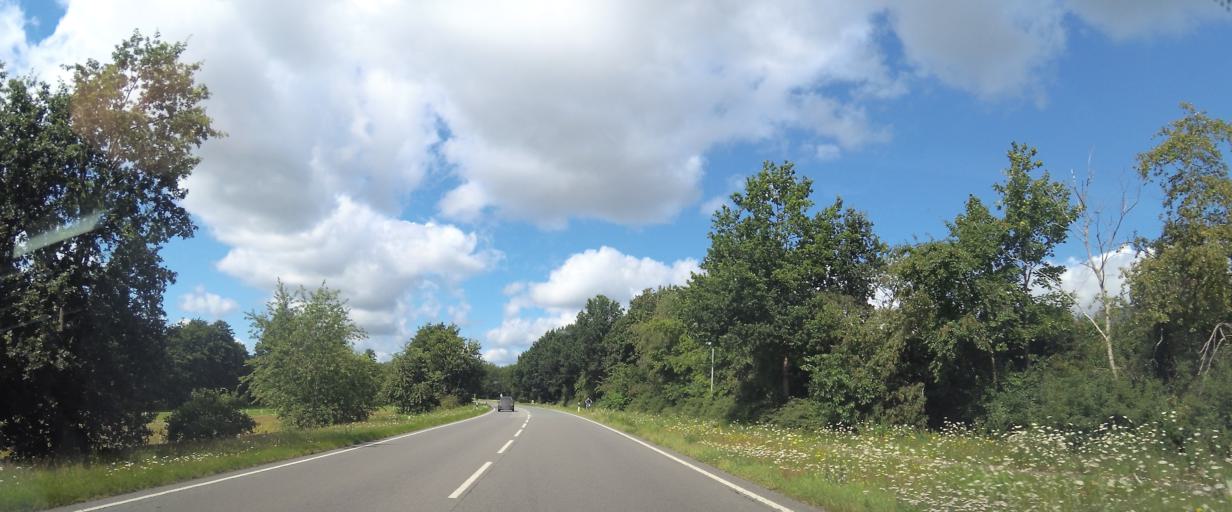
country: DE
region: Lower Saxony
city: Haren
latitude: 52.7888
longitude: 7.2718
